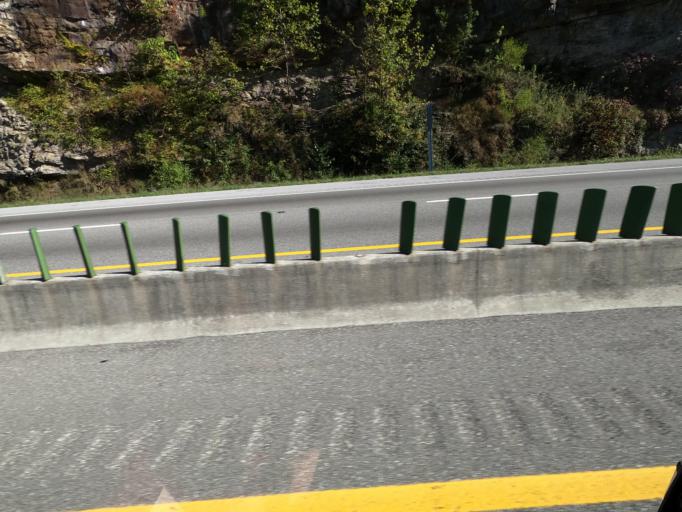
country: US
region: Tennessee
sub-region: Marion County
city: Monteagle
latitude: 35.2394
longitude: -85.8648
